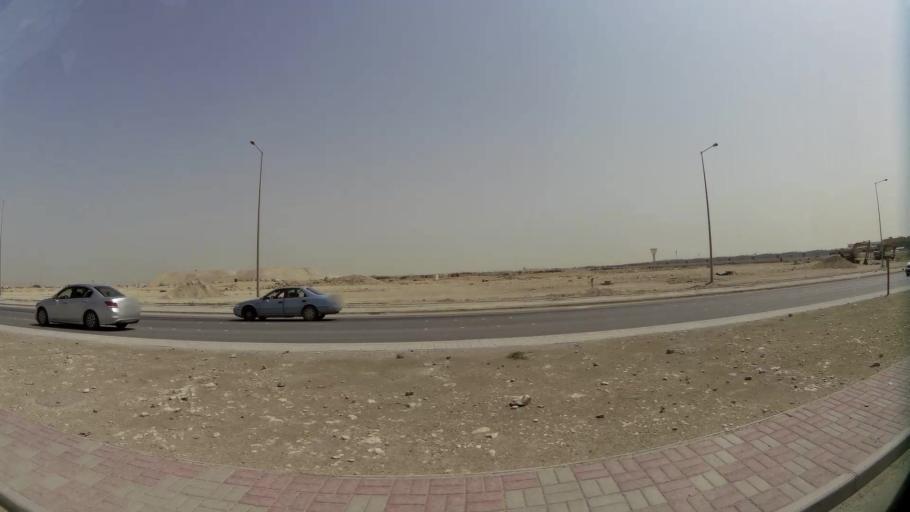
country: QA
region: Baladiyat ar Rayyan
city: Ar Rayyan
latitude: 25.1707
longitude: 51.4006
